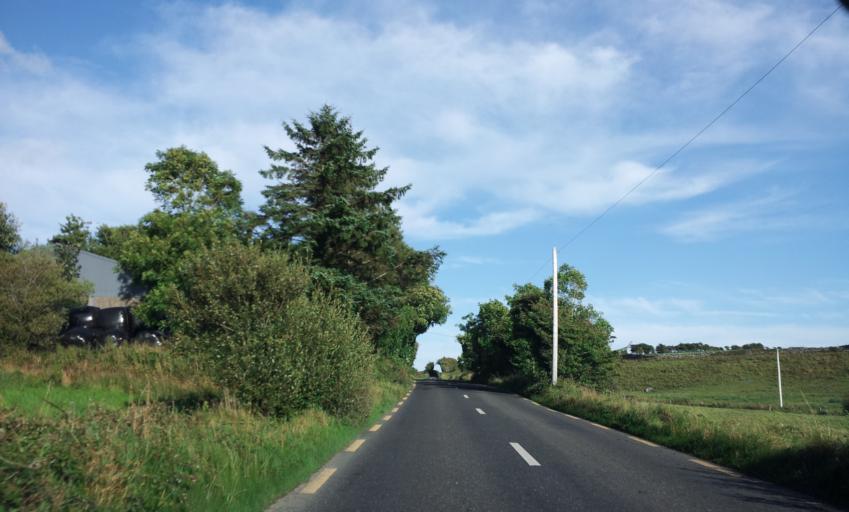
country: IE
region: Munster
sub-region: An Clar
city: Ennis
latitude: 52.9844
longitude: -9.1340
